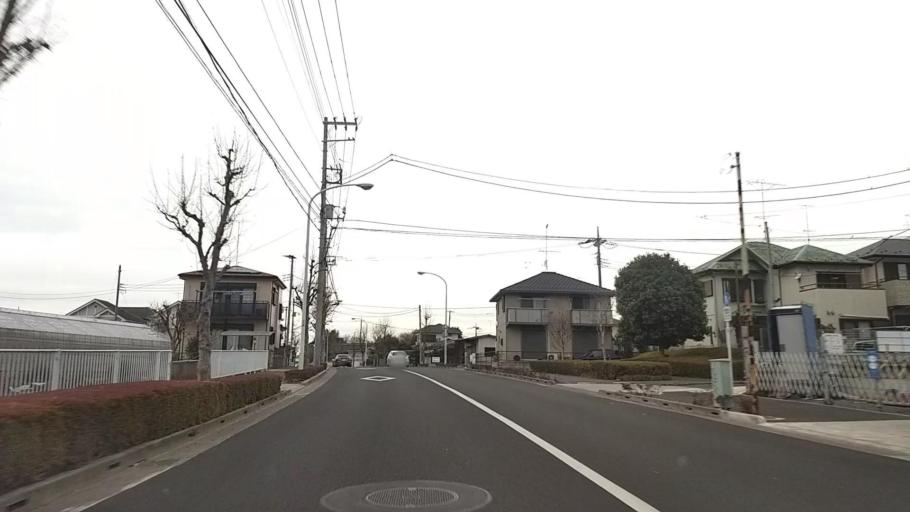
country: JP
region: Tokyo
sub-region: Machida-shi
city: Machida
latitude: 35.5237
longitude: 139.4613
